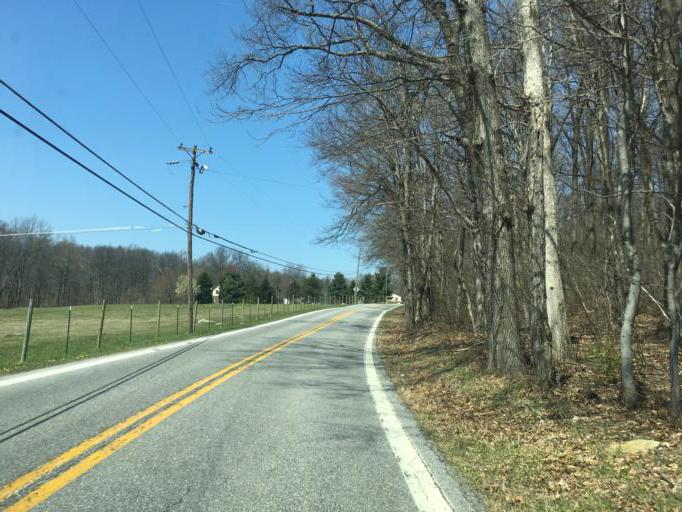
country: US
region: Maryland
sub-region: Washington County
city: Cavetown
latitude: 39.6148
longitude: -77.5578
